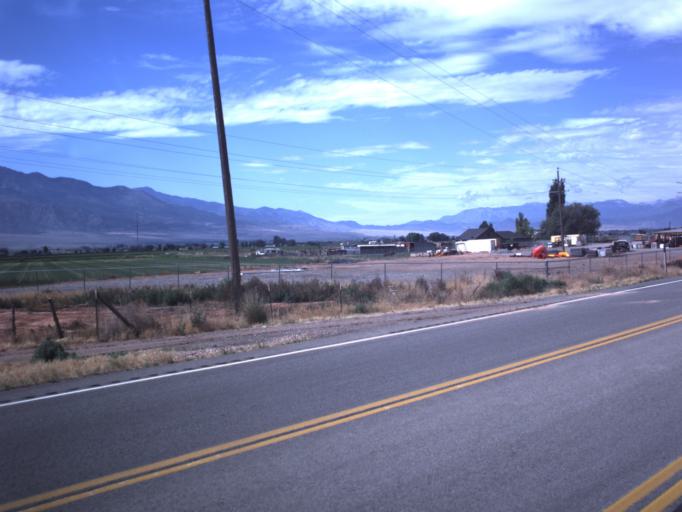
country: US
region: Utah
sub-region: Sevier County
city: Richfield
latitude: 38.7926
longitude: -112.0415
